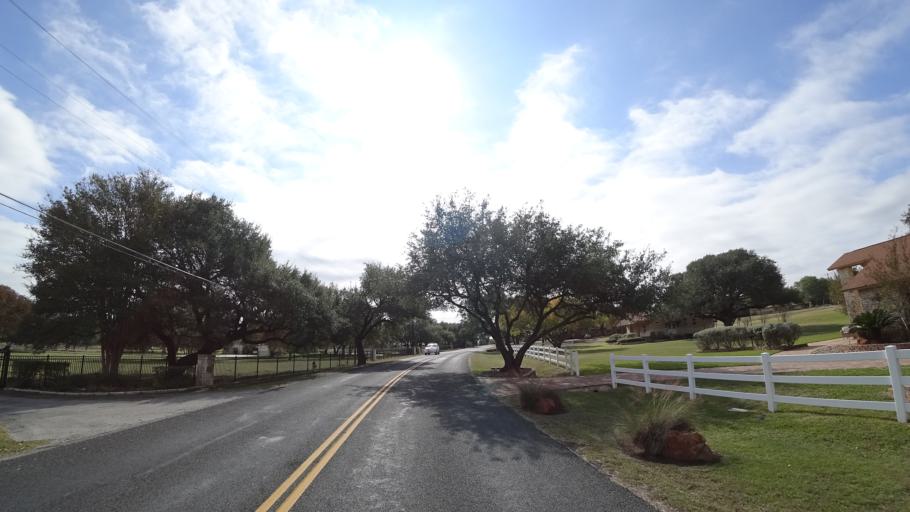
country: US
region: Texas
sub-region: Williamson County
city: Brushy Creek
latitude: 30.5279
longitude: -97.7368
